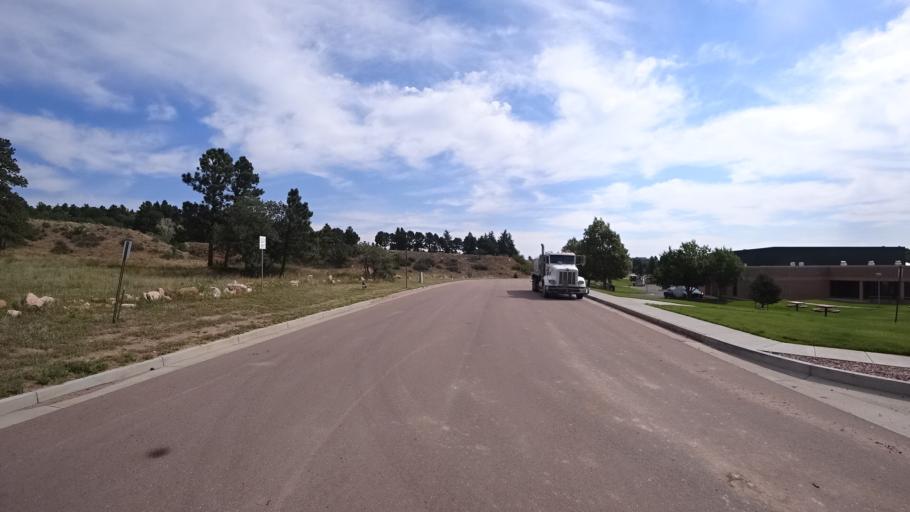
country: US
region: Colorado
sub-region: El Paso County
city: Air Force Academy
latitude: 38.9461
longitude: -104.8711
